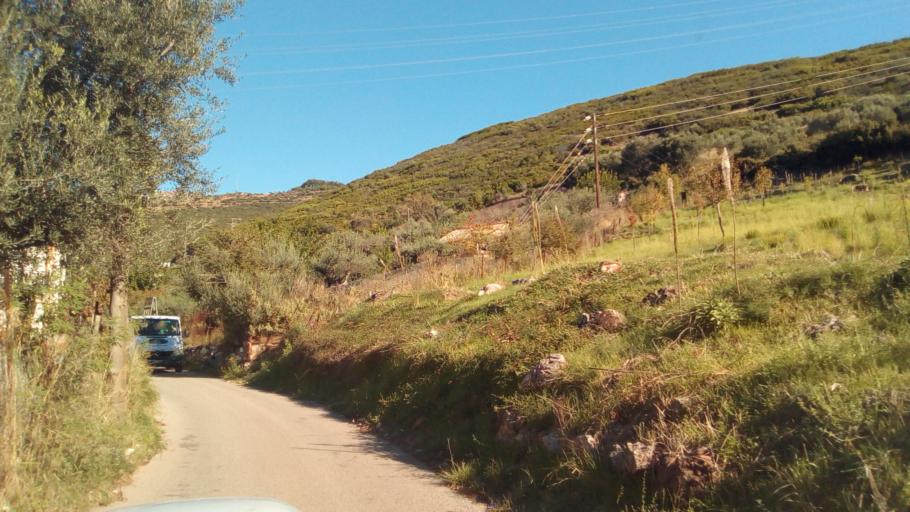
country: GR
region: West Greece
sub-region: Nomos Aitolias kai Akarnanias
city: Nafpaktos
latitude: 38.4049
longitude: 21.8564
